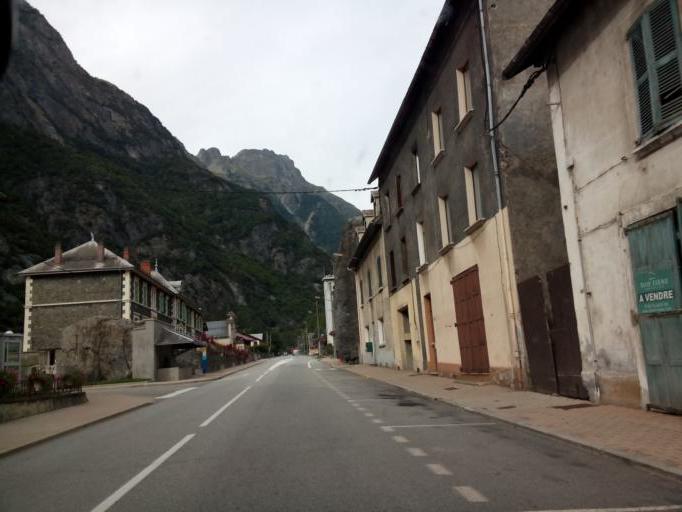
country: FR
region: Rhone-Alpes
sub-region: Departement de l'Isere
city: Livet-et-Gavet
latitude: 45.0916
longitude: 5.9031
